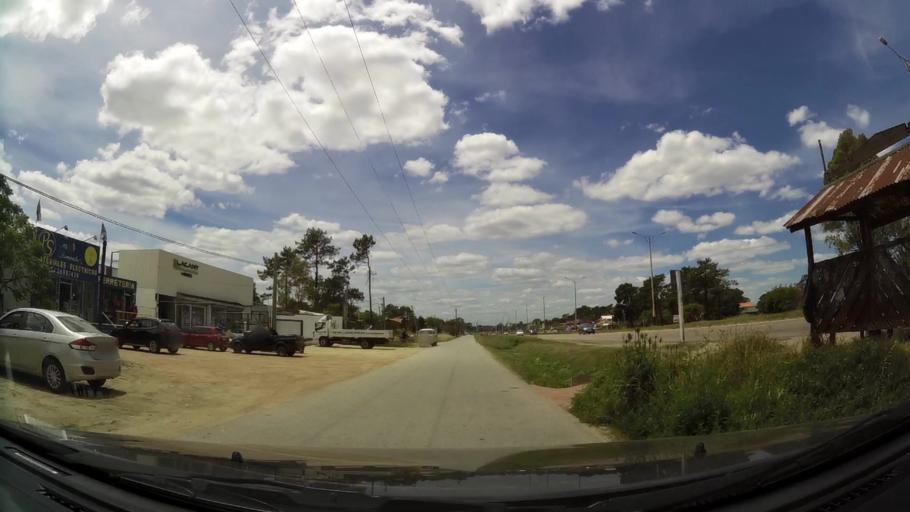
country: UY
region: Canelones
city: Pando
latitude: -34.8032
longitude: -55.9252
